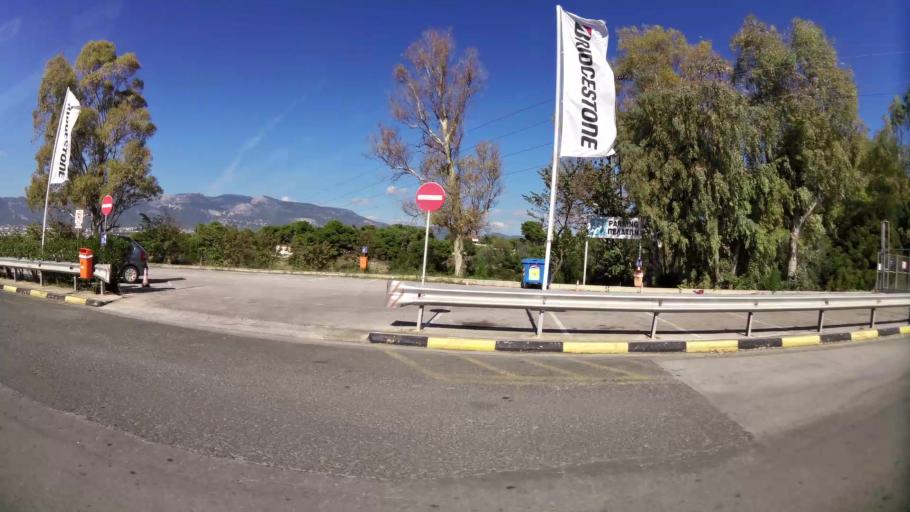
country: GR
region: Attica
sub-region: Nomarchia Athinas
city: Lykovrysi
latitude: 38.0901
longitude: 23.7860
